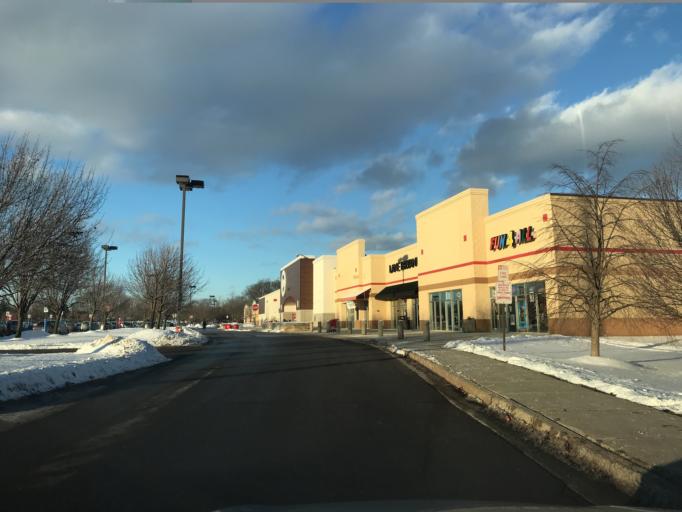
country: US
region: Michigan
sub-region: Washtenaw County
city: Ypsilanti
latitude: 42.2345
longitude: -83.6775
